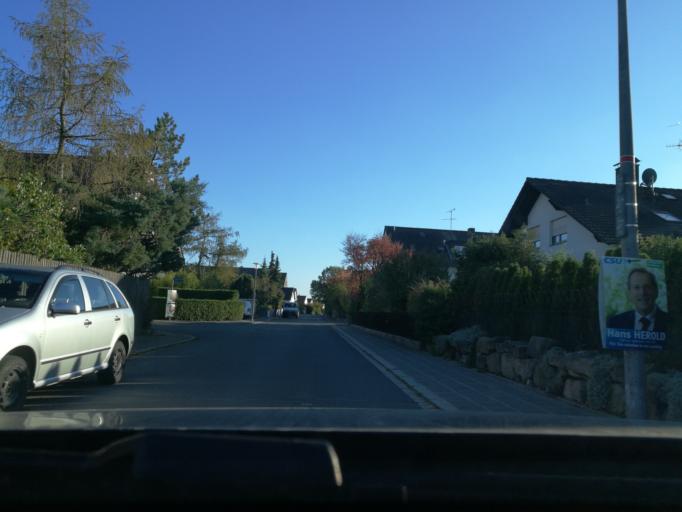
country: DE
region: Bavaria
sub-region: Regierungsbezirk Mittelfranken
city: Seukendorf
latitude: 49.4885
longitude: 10.8815
